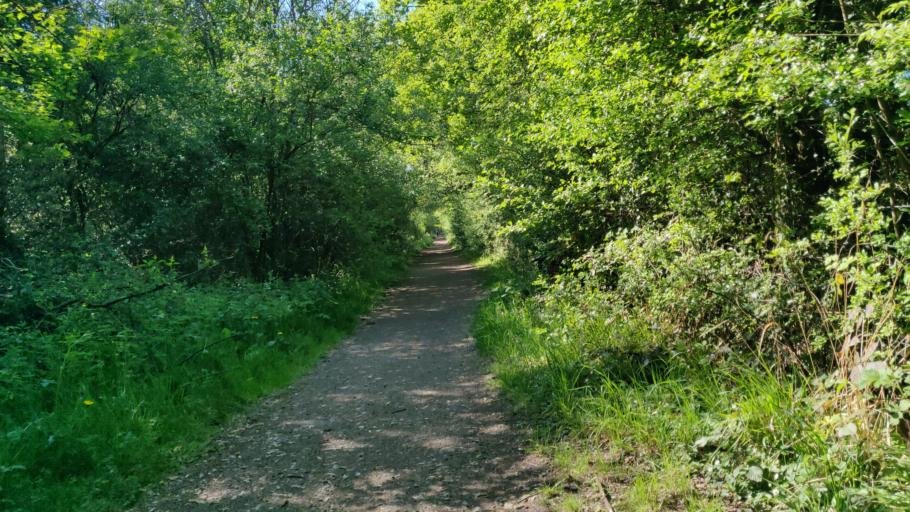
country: GB
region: England
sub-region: West Sussex
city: Rudgwick
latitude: 51.0641
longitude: -0.3999
